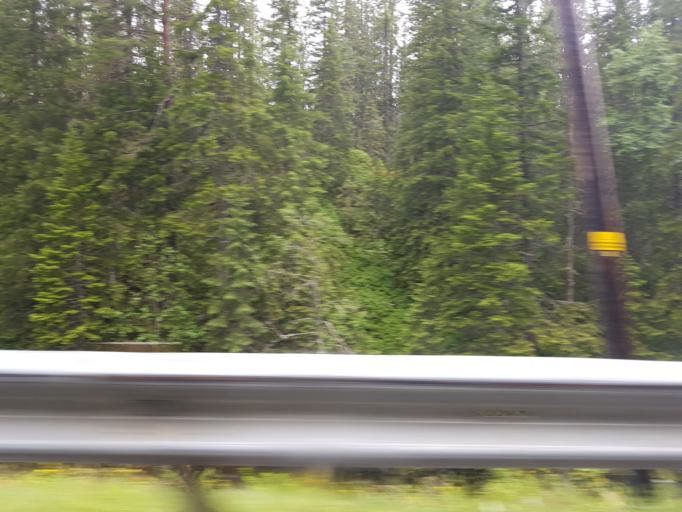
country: NO
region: Sor-Trondelag
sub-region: Selbu
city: Mebonden
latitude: 63.3571
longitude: 11.0767
